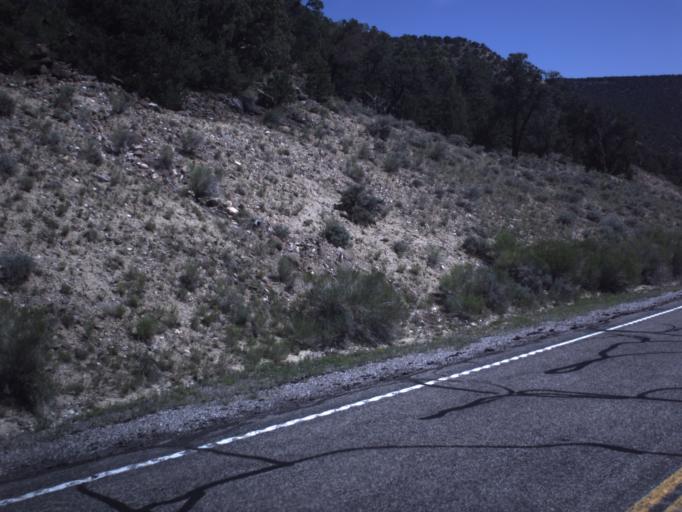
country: US
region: Utah
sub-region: Wayne County
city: Loa
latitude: 38.6620
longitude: -111.4293
